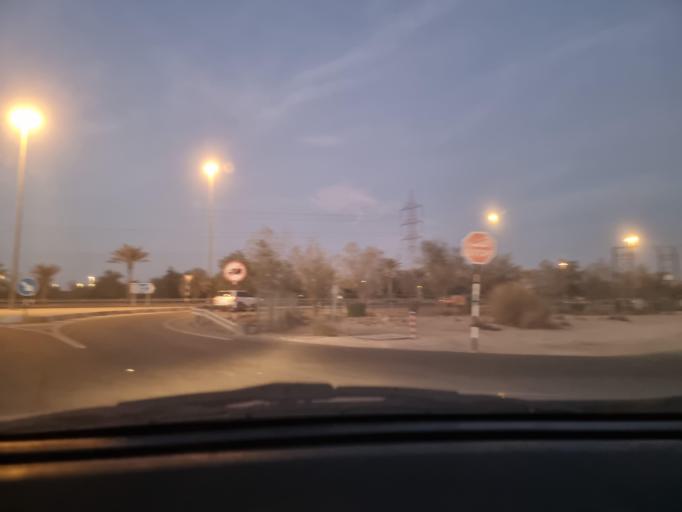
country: AE
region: Abu Dhabi
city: Al Ain
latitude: 24.2045
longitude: 55.4256
